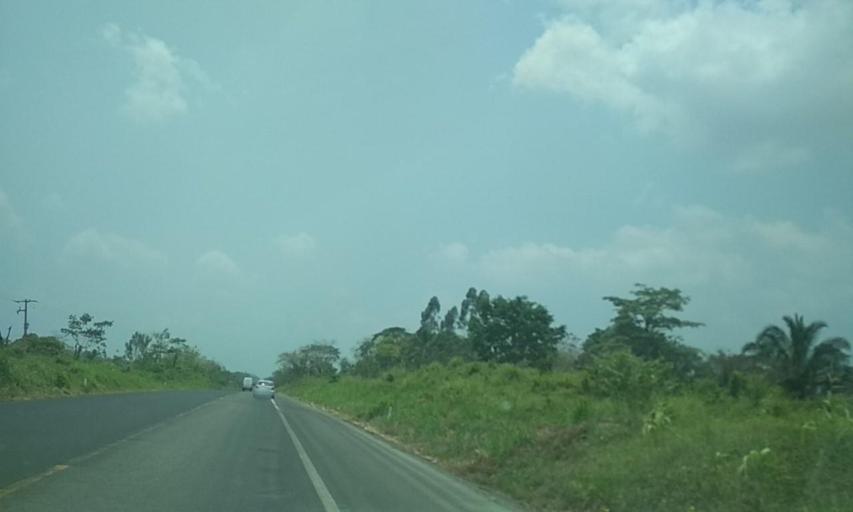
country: MX
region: Tabasco
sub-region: Huimanguillo
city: Francisco Rueda
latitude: 17.7000
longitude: -93.9257
